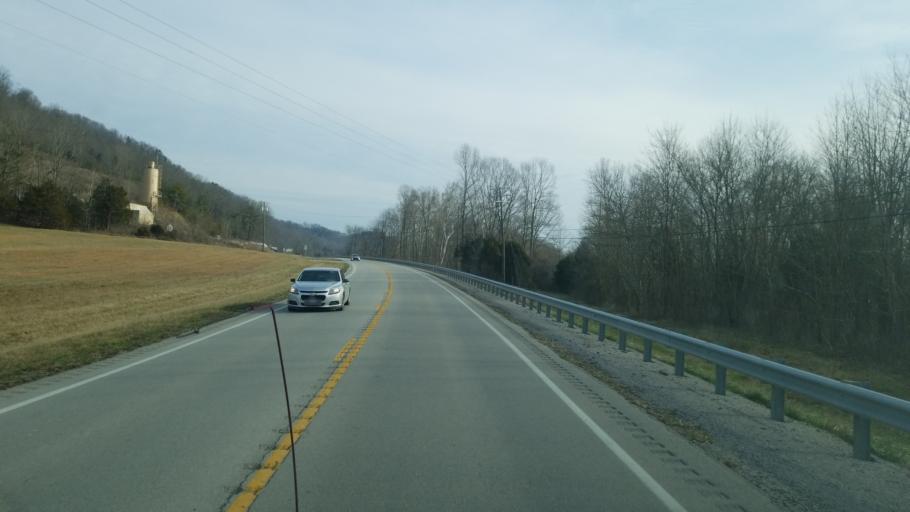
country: US
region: Kentucky
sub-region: Casey County
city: Liberty
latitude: 37.3395
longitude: -84.9017
